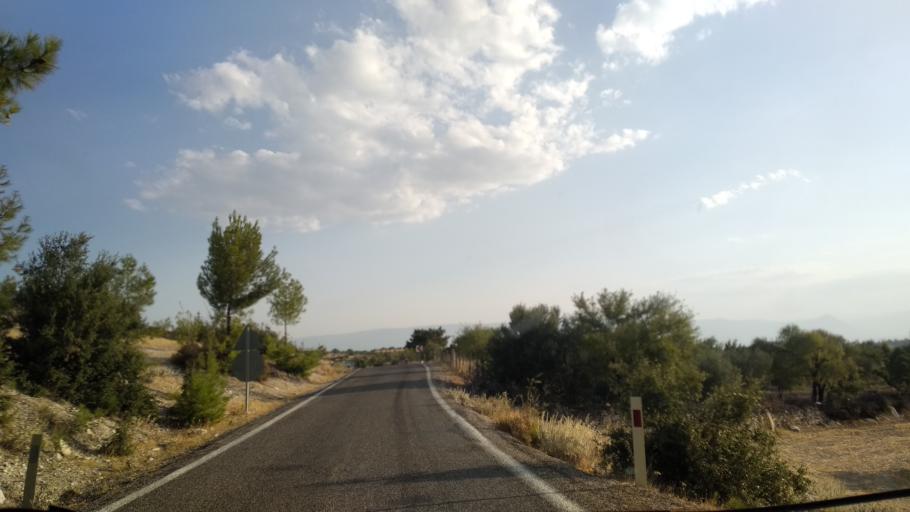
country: TR
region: Mersin
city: Sarikavak
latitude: 36.5740
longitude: 33.6387
